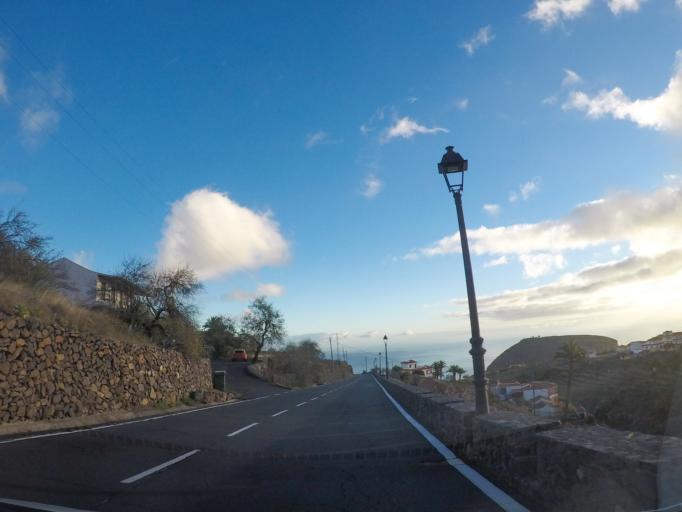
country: ES
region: Canary Islands
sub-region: Provincia de Santa Cruz de Tenerife
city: Alajero
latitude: 28.0635
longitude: -17.2371
